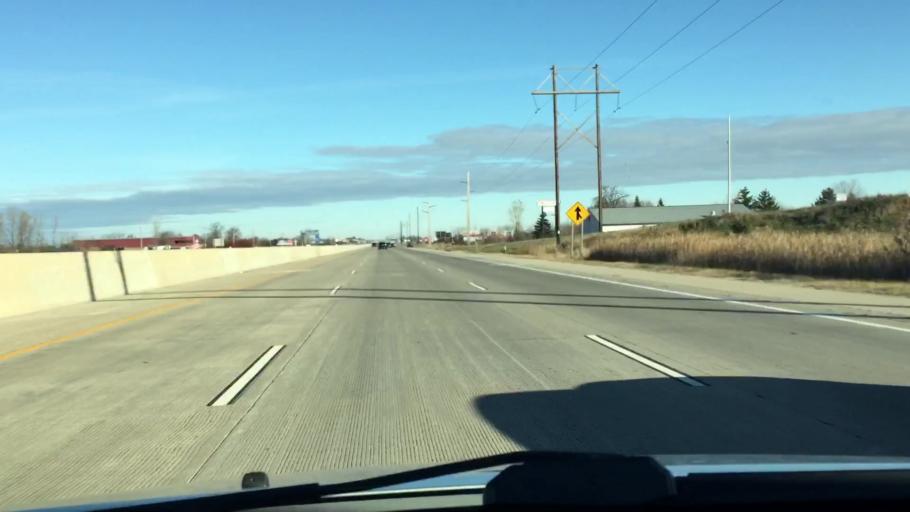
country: US
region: Wisconsin
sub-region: Winnebago County
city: Oshkosh
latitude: 43.9515
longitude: -88.5831
